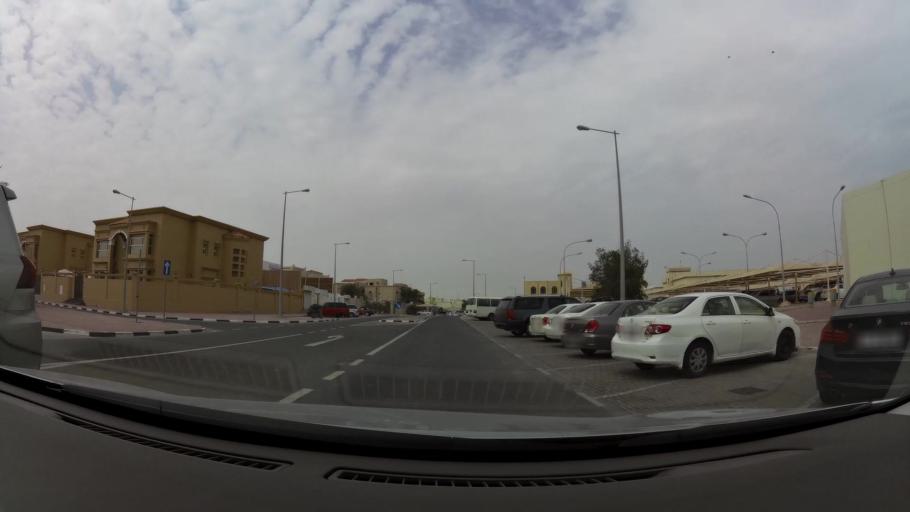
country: QA
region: Baladiyat ar Rayyan
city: Ar Rayyan
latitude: 25.3306
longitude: 51.4767
